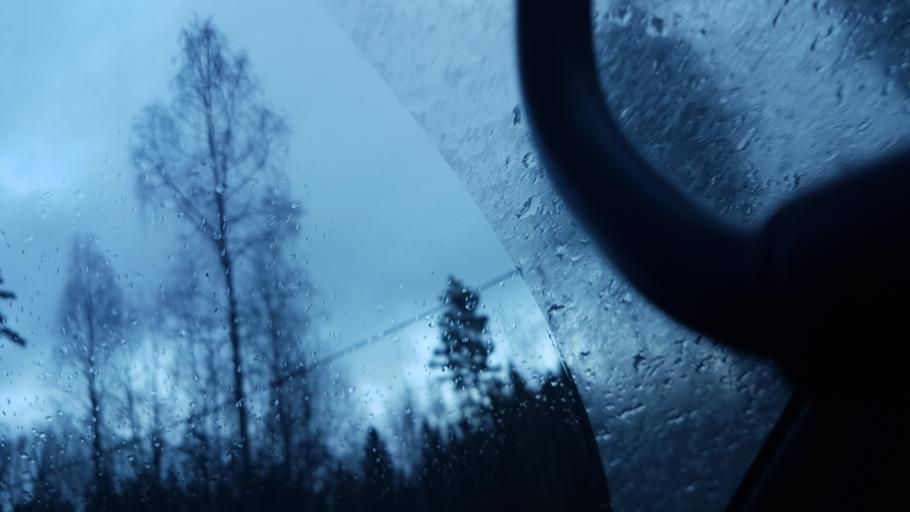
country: FI
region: Uusimaa
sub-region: Helsinki
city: Lohja
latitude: 60.2146
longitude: 24.0904
